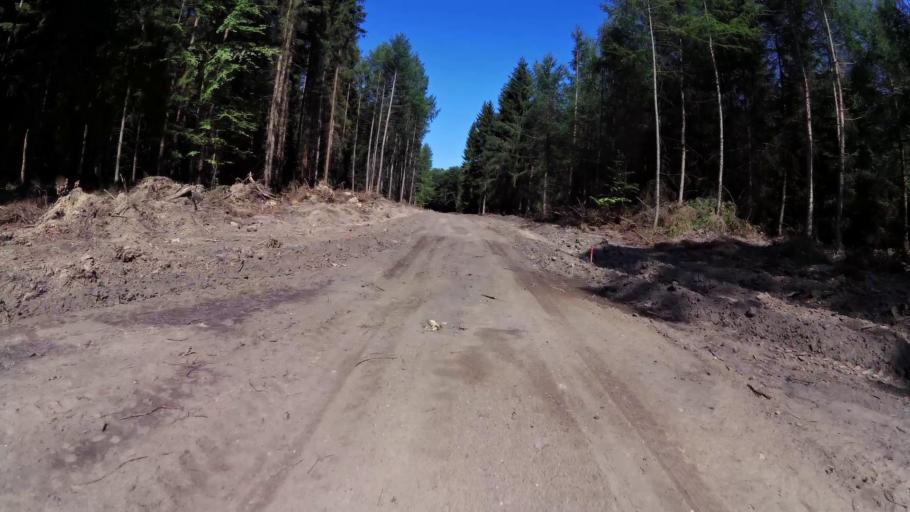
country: PL
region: West Pomeranian Voivodeship
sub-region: Powiat drawski
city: Wierzchowo
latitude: 53.4108
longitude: 16.2332
